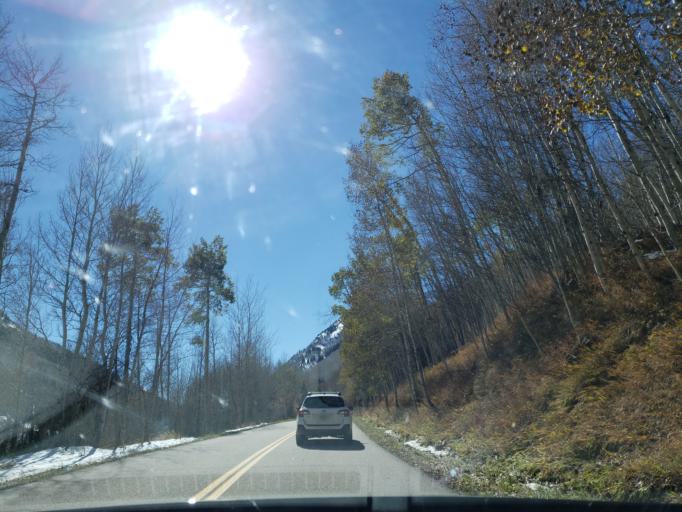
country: US
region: Colorado
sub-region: Pitkin County
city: Snowmass Village
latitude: 39.1145
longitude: -106.9120
